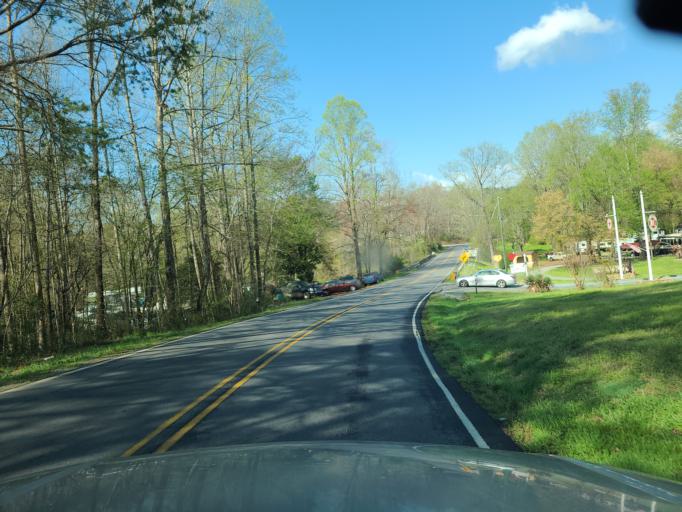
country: US
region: North Carolina
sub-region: Rutherford County
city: Spindale
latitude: 35.3841
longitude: -81.9185
